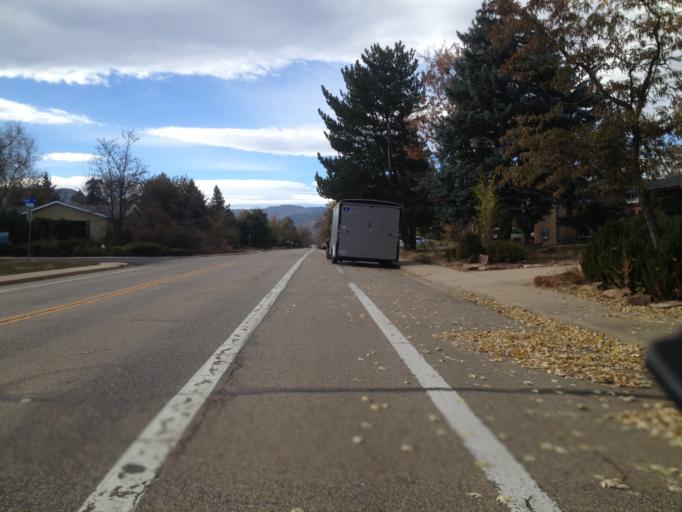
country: US
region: Colorado
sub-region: Boulder County
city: Boulder
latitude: 39.9905
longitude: -105.2433
